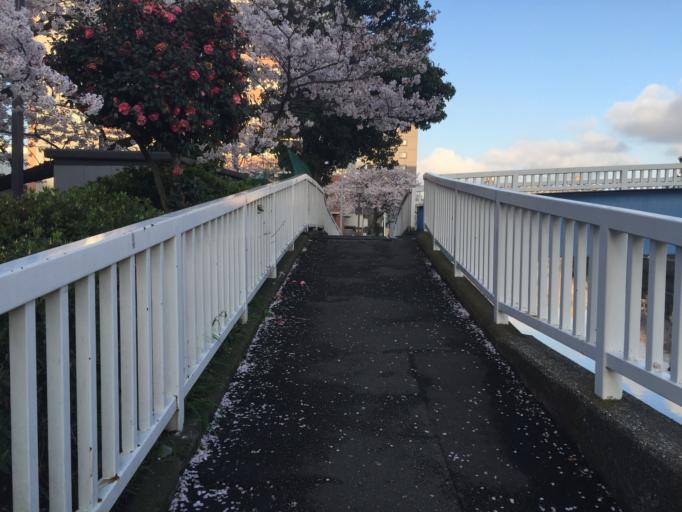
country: JP
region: Kanagawa
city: Yokohama
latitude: 35.4387
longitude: 139.6219
